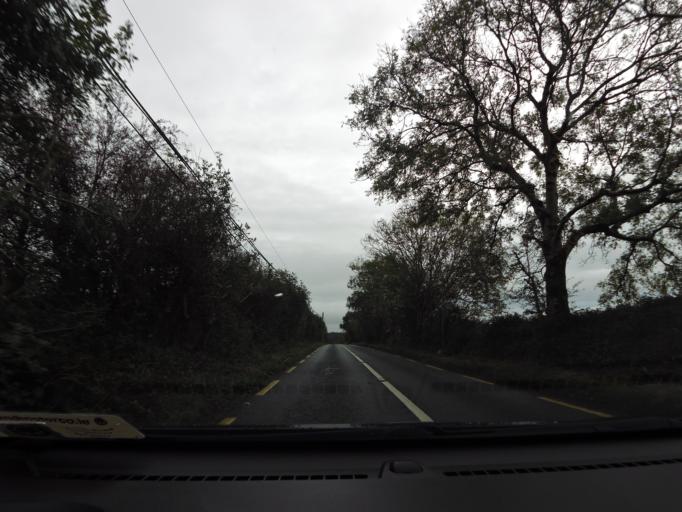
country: IE
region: Connaught
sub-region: County Galway
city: Tuam
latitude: 53.5506
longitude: -8.8079
